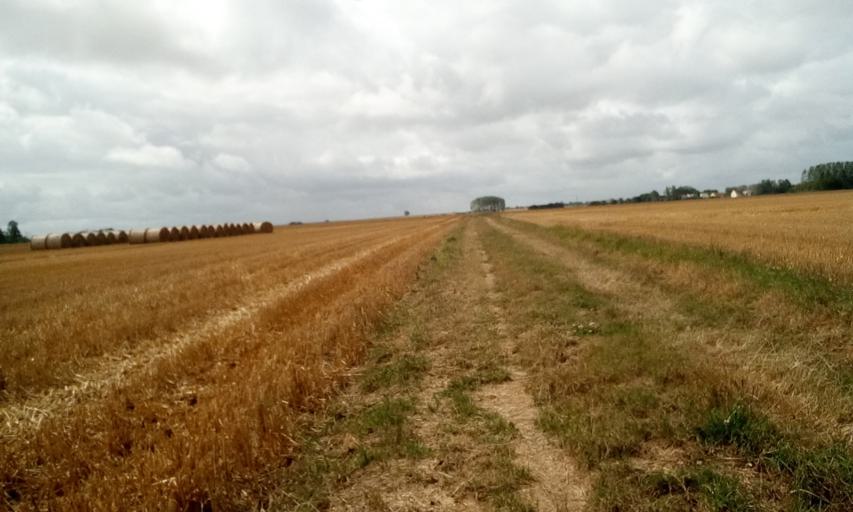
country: FR
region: Lower Normandy
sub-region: Departement du Calvados
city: Cheux
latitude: 49.1908
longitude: -0.5302
